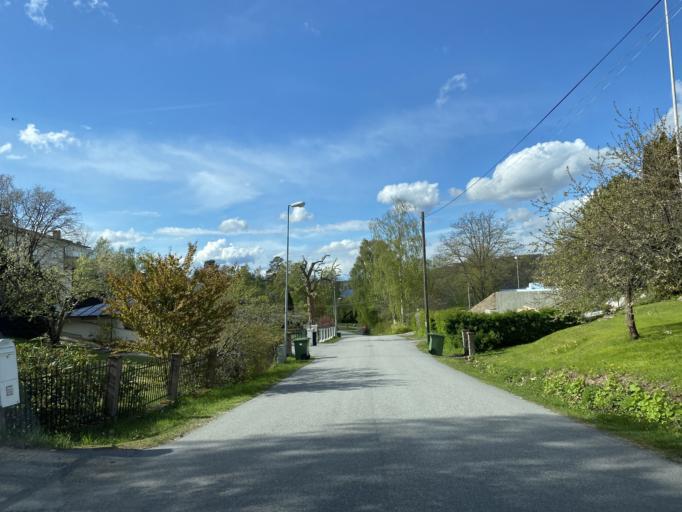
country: SE
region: Stockholm
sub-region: Sollentuna Kommun
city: Sollentuna
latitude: 59.4214
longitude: 17.9783
